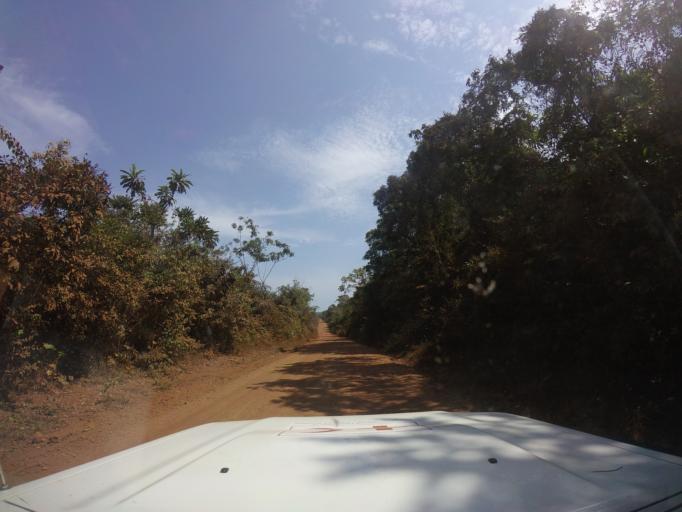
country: LR
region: Grand Cape Mount
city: Robertsport
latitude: 6.7171
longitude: -11.3367
